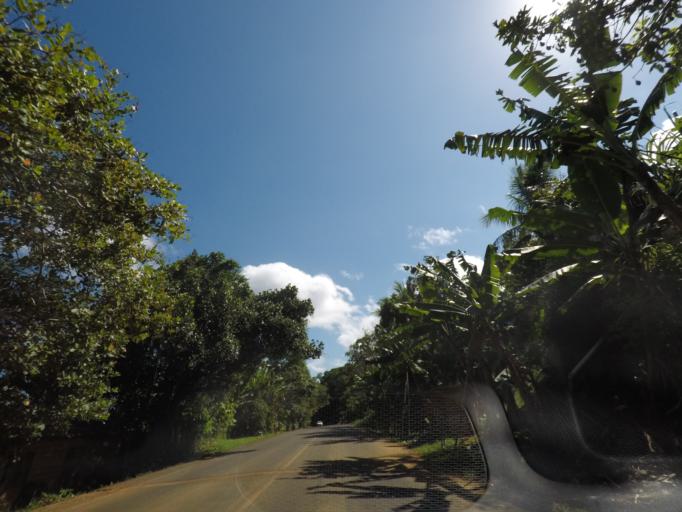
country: BR
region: Bahia
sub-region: Itubera
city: Itubera
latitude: -13.7611
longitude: -39.1523
